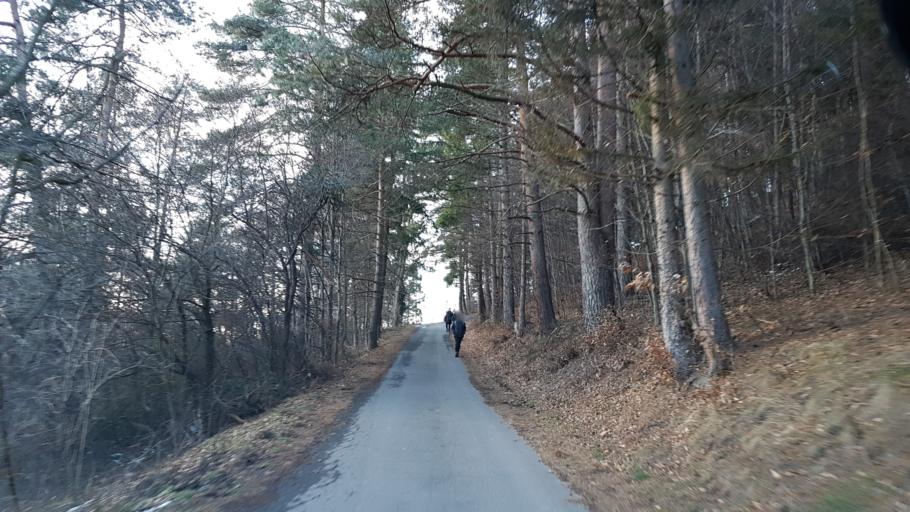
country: PL
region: Lesser Poland Voivodeship
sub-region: Powiat nowosadecki
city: Rytro
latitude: 49.4893
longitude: 20.6899
